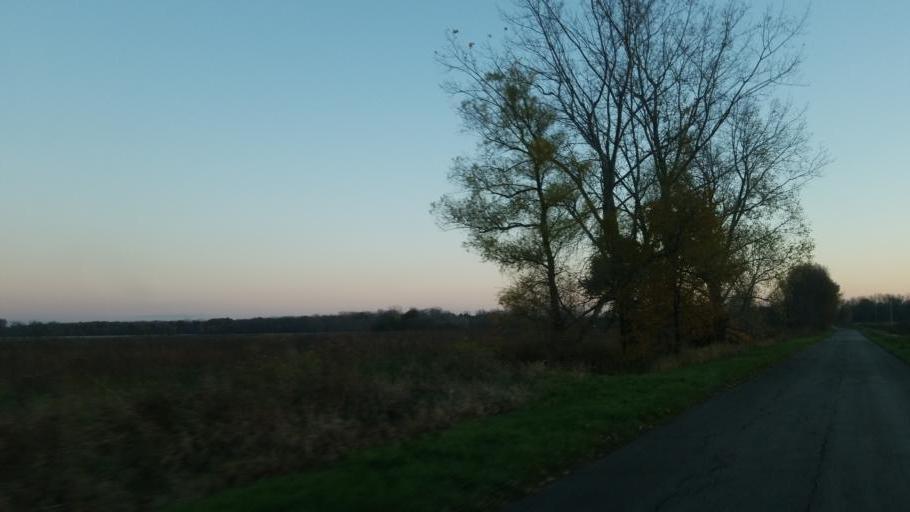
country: US
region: Ohio
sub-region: Huron County
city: Willard
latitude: 41.0291
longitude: -82.7818
